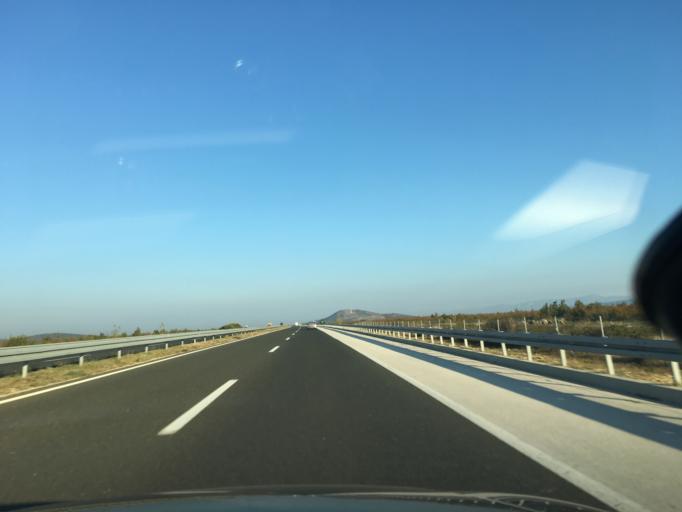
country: HR
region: Sibensko-Kniniska
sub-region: Grad Sibenik
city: Pirovac
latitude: 43.9140
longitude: 15.7482
